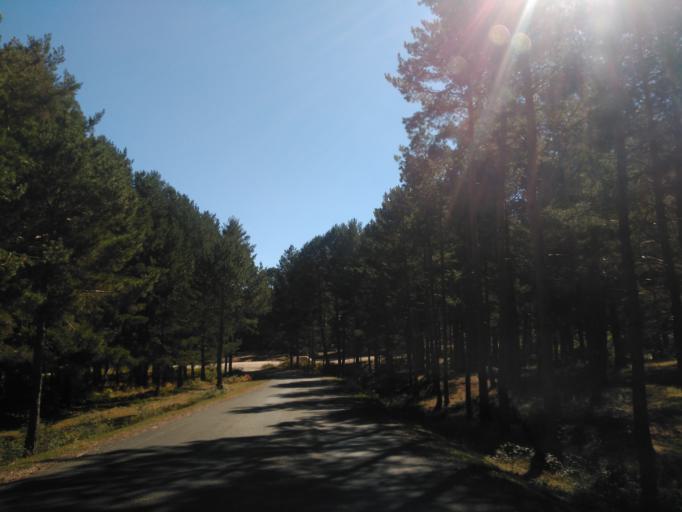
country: ES
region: Castille and Leon
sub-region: Provincia de Soria
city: Vinuesa
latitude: 41.9635
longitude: -2.7890
